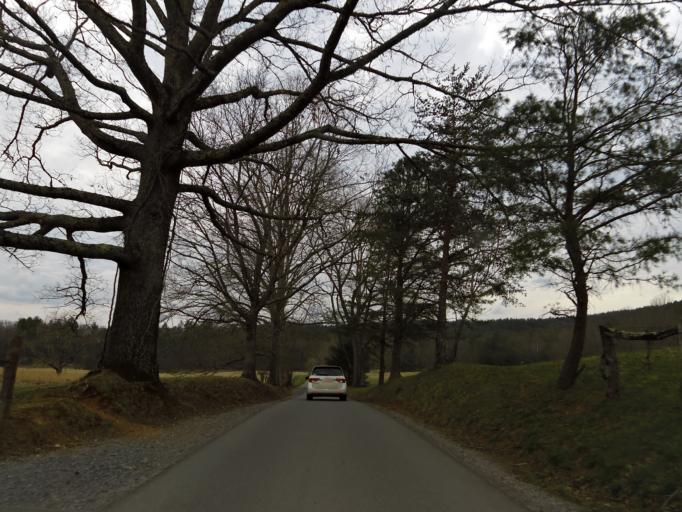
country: US
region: Tennessee
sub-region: Blount County
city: Wildwood
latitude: 35.6072
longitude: -83.8186
